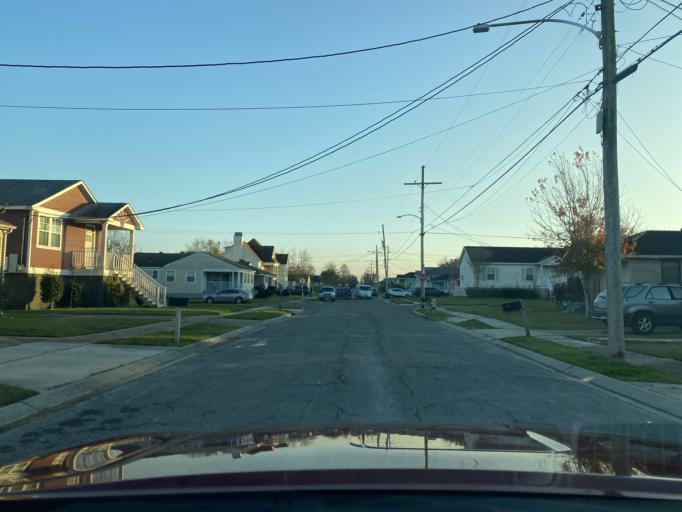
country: US
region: Louisiana
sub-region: Orleans Parish
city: New Orleans
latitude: 30.0209
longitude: -90.0506
